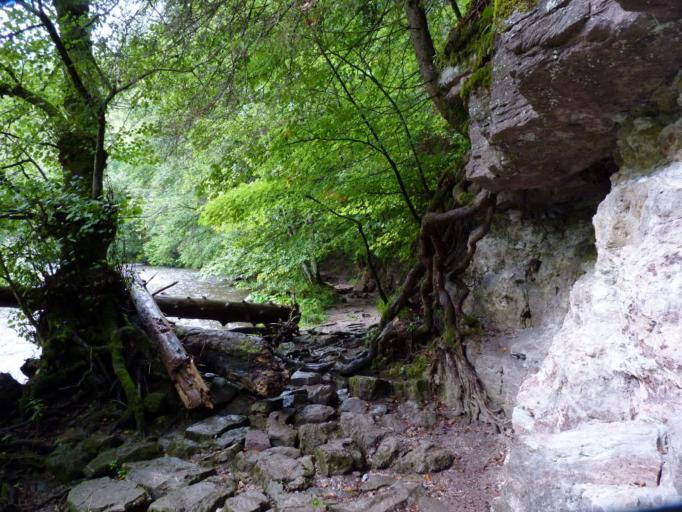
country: DE
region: Baden-Wuerttemberg
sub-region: Freiburg Region
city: Bonndorf im Schwarzwald
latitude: 47.8439
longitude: 8.3273
